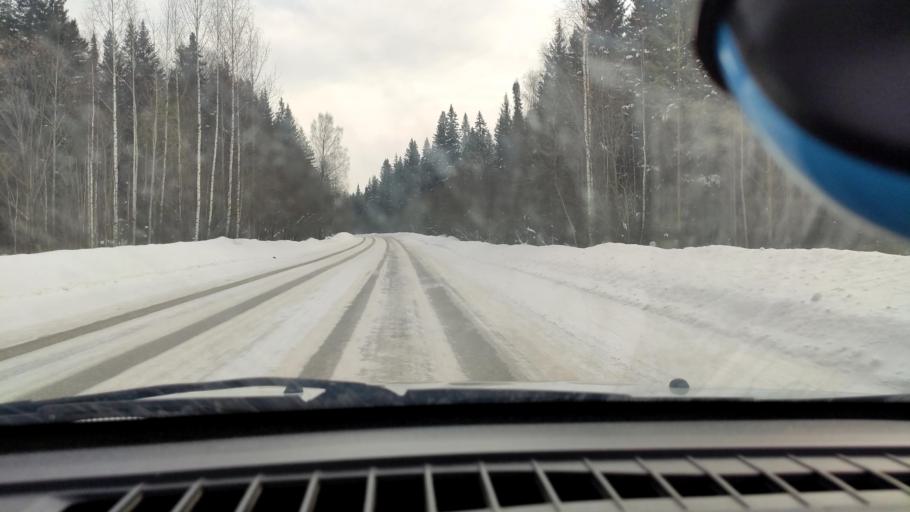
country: RU
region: Perm
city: Overyata
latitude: 58.1059
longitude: 55.8385
